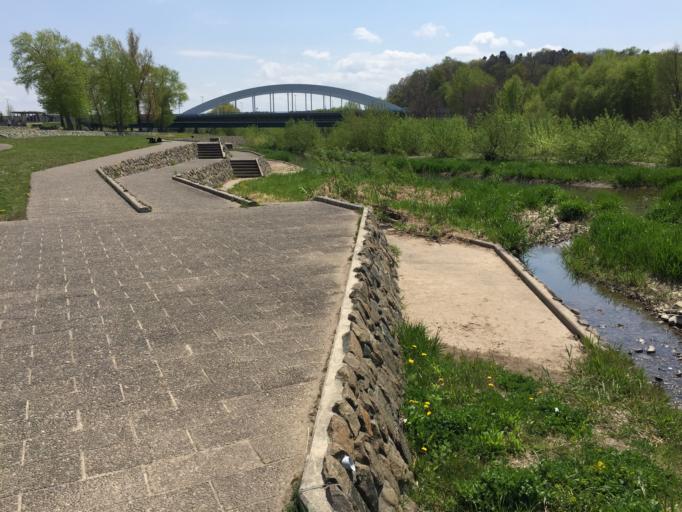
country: JP
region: Hokkaido
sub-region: Asahikawa-shi
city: Asahikawa
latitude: 43.7574
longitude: 142.3647
